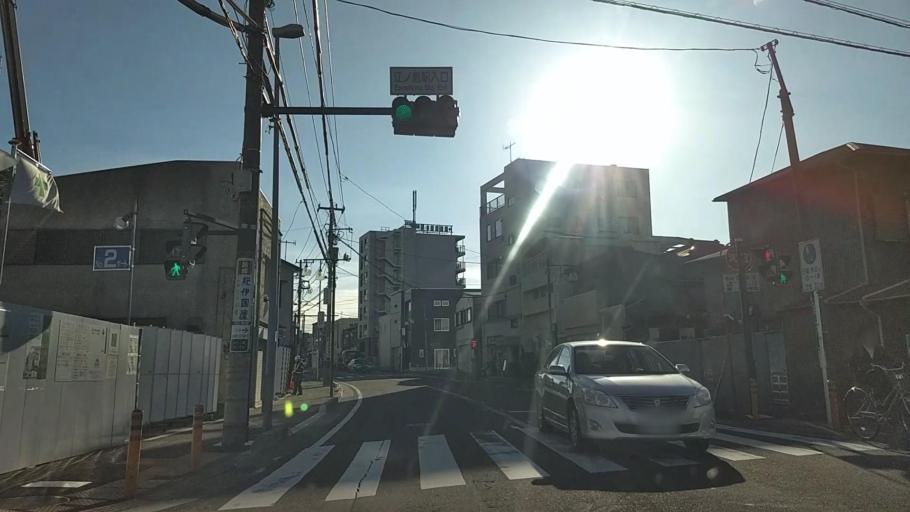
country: JP
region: Kanagawa
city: Fujisawa
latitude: 35.3116
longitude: 139.4872
